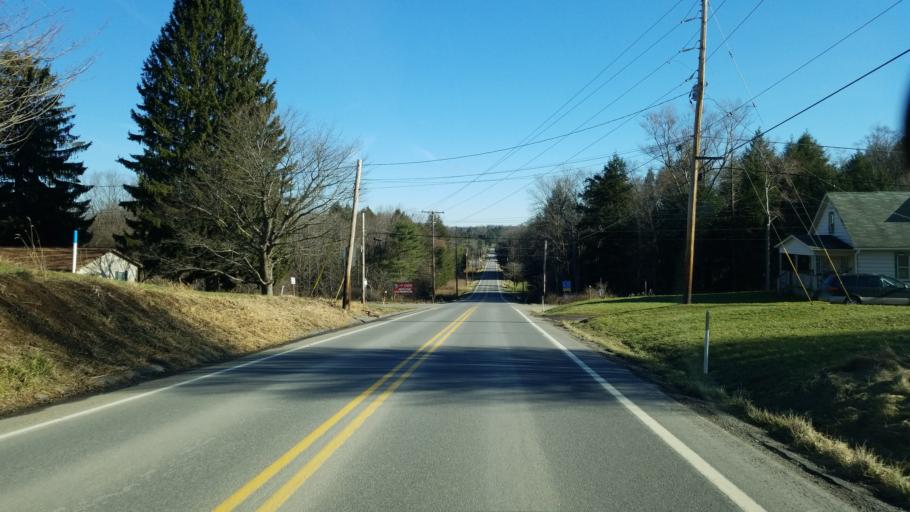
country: US
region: Pennsylvania
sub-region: Jefferson County
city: Falls Creek
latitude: 41.1776
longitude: -78.8564
